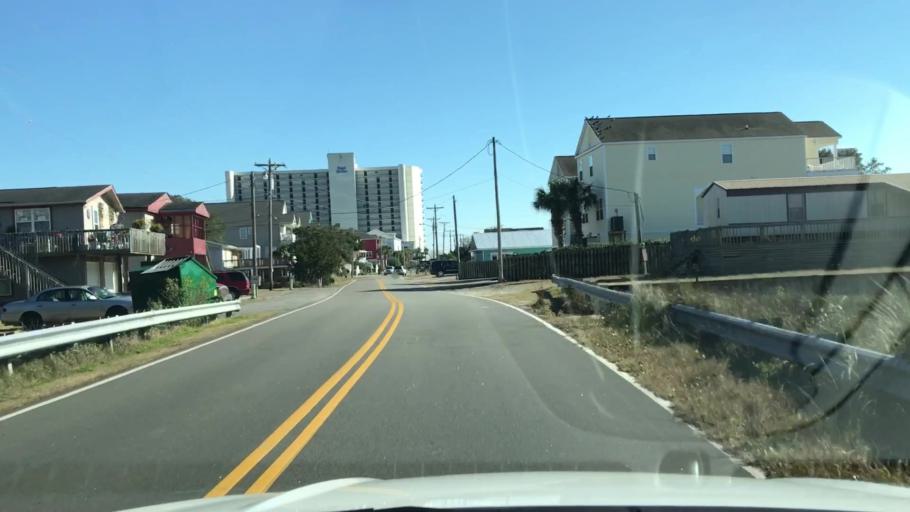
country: US
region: South Carolina
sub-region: Horry County
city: Garden City
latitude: 33.5875
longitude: -78.9935
